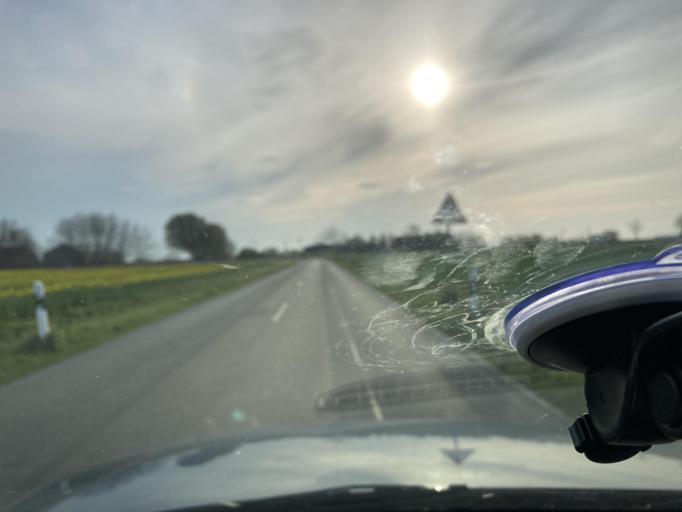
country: DE
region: Schleswig-Holstein
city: Schulp
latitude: 54.2537
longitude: 8.9472
